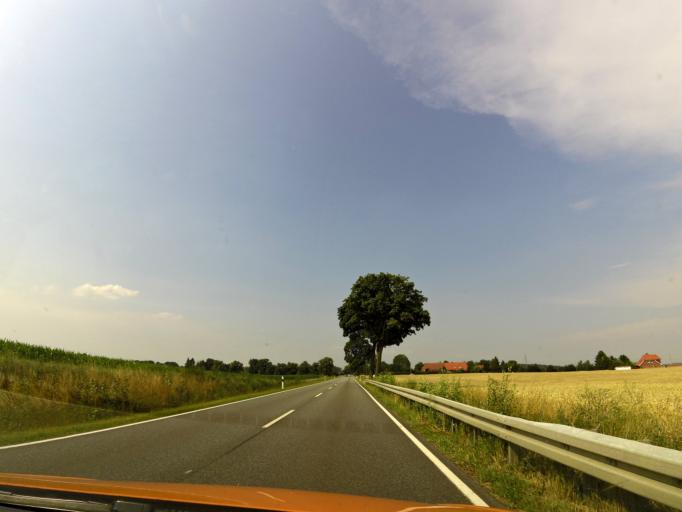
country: DE
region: Mecklenburg-Vorpommern
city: Krakow am See
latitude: 53.7241
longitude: 12.2773
